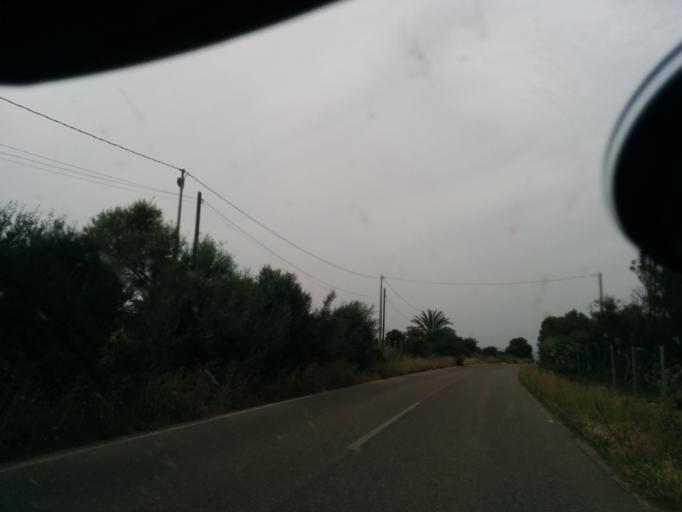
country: IT
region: Sardinia
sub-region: Provincia di Carbonia-Iglesias
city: Sant'Antioco
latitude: 39.0335
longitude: 8.4534
